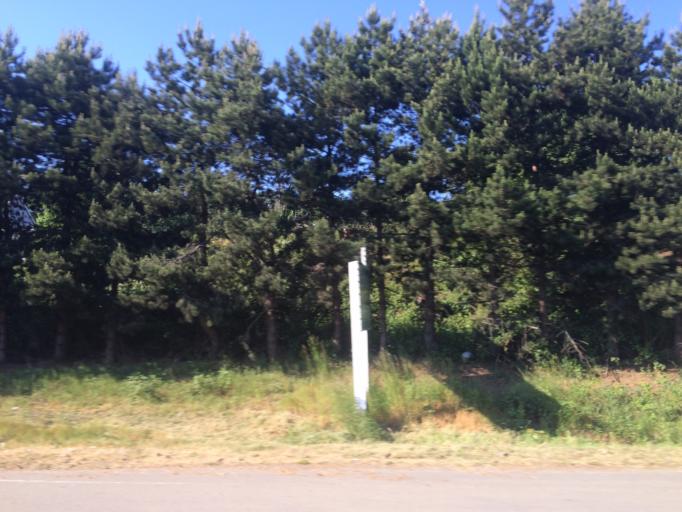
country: CA
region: British Columbia
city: Victoria
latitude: 48.4640
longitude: -123.4163
